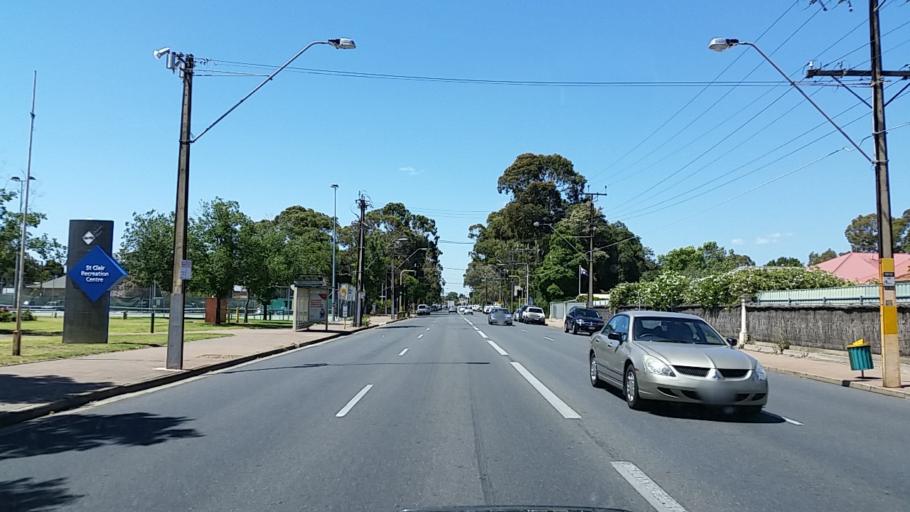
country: AU
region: South Australia
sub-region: Charles Sturt
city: Woodville North
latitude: -34.8753
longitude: 138.5404
